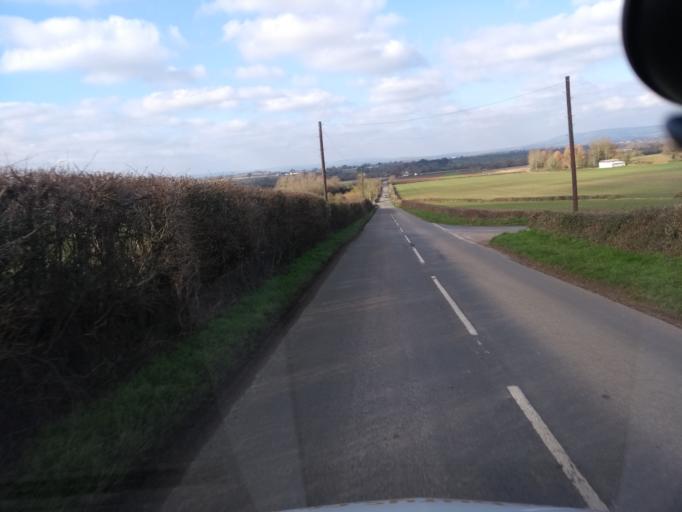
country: GB
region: England
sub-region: Somerset
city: Creech Saint Michael
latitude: 50.9815
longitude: -3.0570
